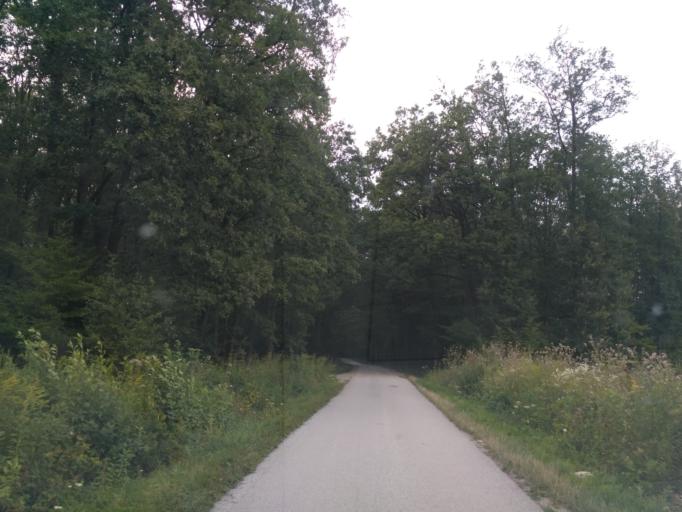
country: SK
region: Kosicky
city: Kosice
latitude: 48.7277
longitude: 21.1826
